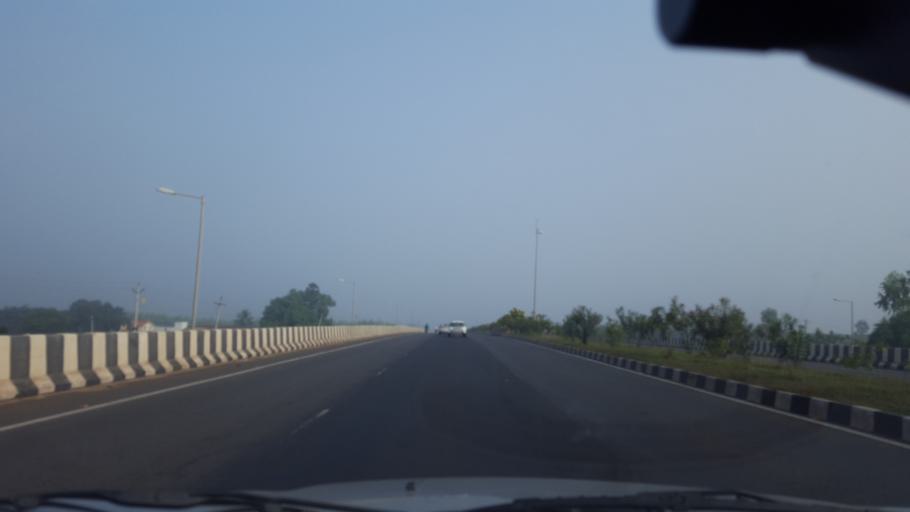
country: IN
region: Andhra Pradesh
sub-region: Prakasam
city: Ongole
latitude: 15.3897
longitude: 80.0393
